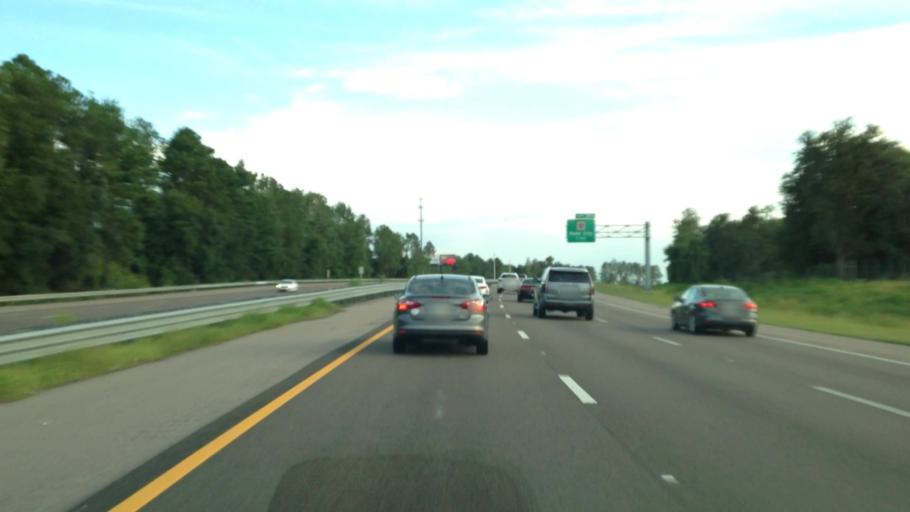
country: US
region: Florida
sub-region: Hernando County
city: Hill 'n Dale
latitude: 28.4290
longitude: -82.2800
